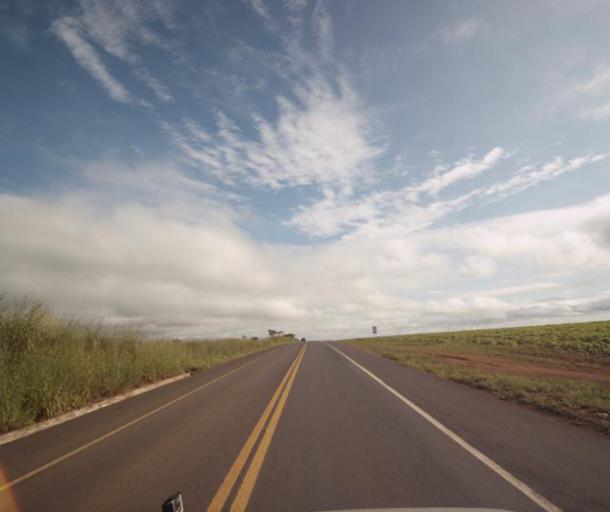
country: BR
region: Goias
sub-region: Padre Bernardo
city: Padre Bernardo
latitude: -15.4306
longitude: -48.6211
